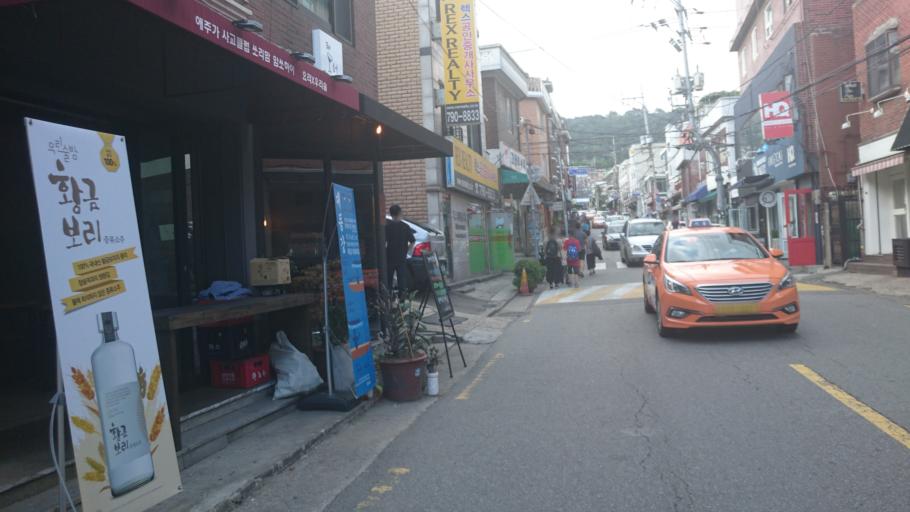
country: KR
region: Seoul
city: Seoul
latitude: 37.5408
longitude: 126.9869
